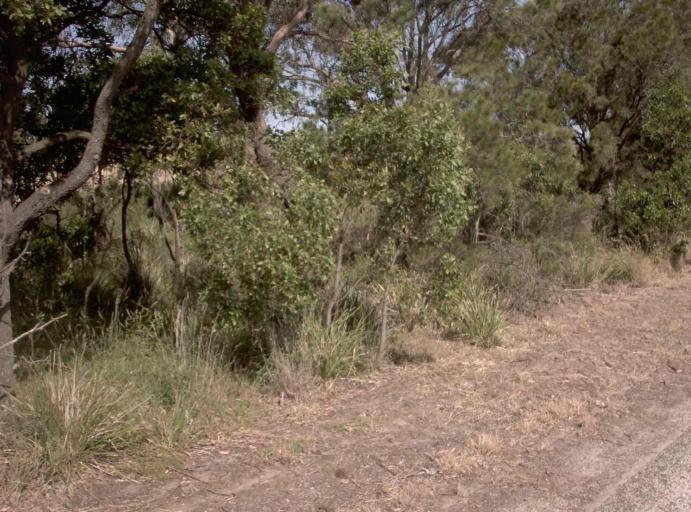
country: AU
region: Victoria
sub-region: Wellington
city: Sale
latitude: -38.3107
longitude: 147.1537
